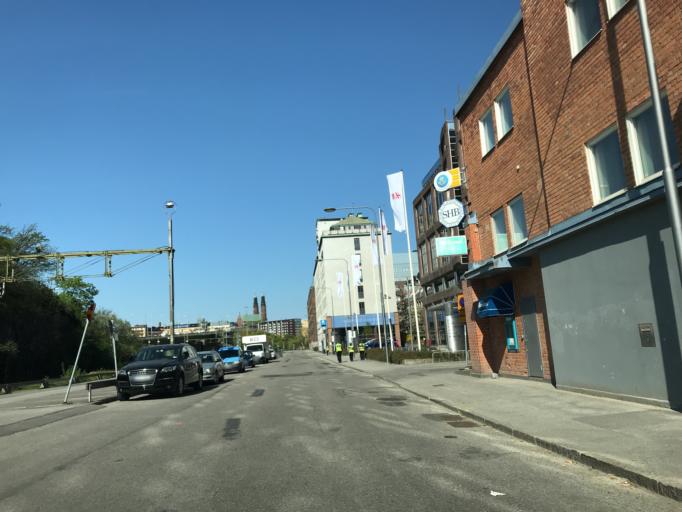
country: SE
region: Stockholm
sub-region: Stockholms Kommun
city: Arsta
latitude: 59.3101
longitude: 18.0285
